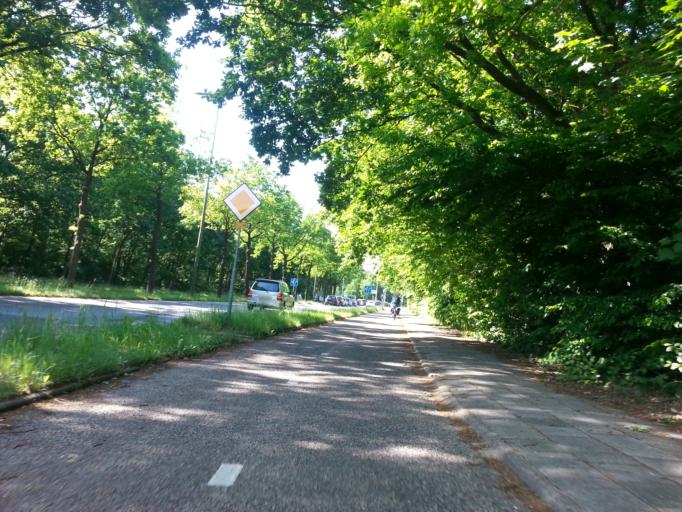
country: NL
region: Utrecht
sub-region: Gemeente Zeist
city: Zeist
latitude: 52.1062
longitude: 5.2377
